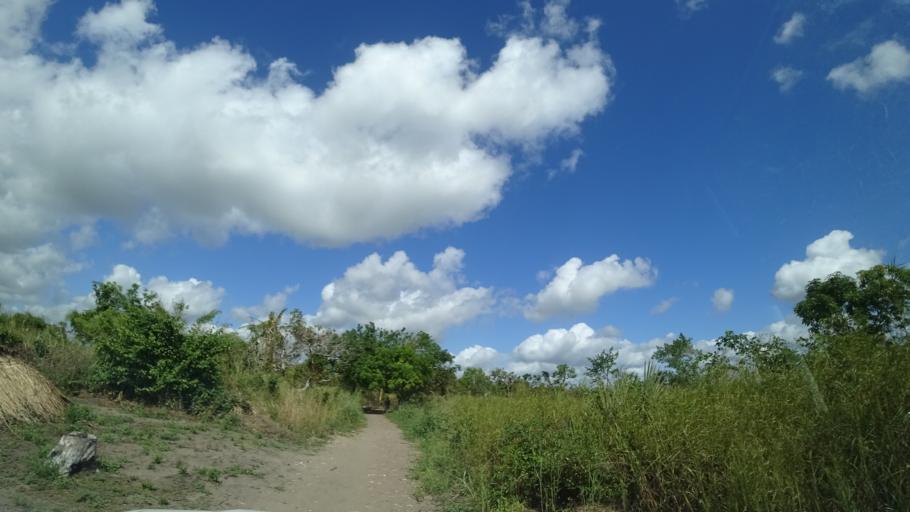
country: MZ
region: Sofala
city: Dondo
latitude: -19.3584
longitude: 34.5787
